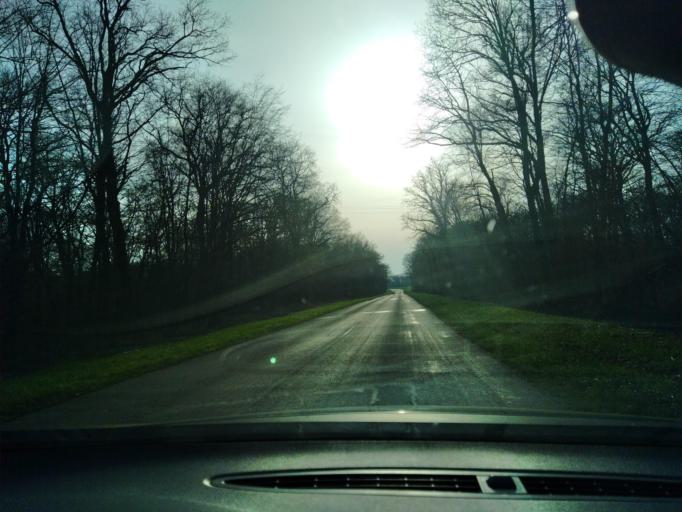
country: FR
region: Franche-Comte
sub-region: Departement du Jura
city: Choisey
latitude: 47.0025
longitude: 5.4809
